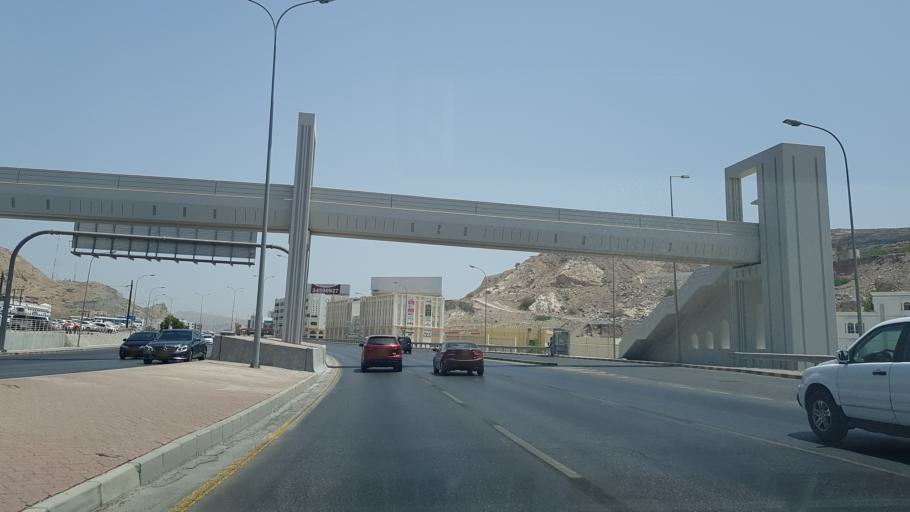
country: OM
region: Muhafazat Masqat
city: Muscat
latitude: 23.6024
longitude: 58.5139
